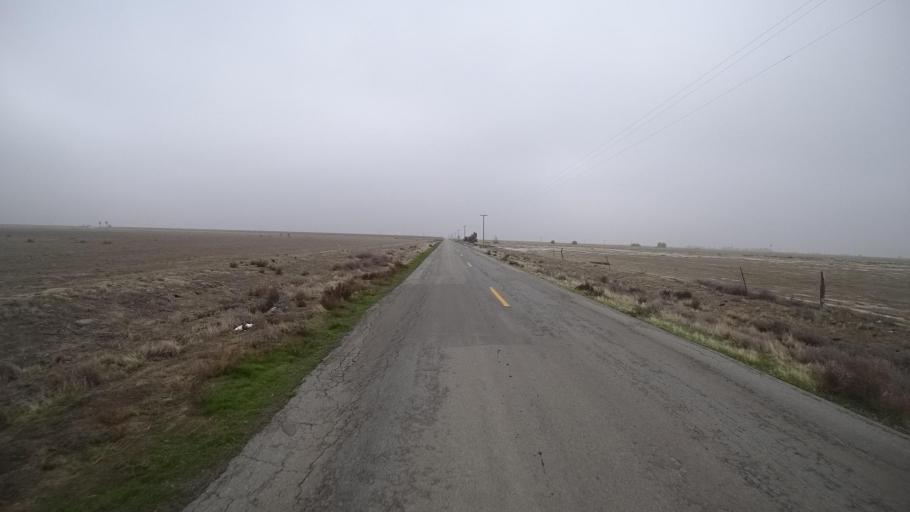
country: US
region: California
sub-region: Tulare County
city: Alpaugh
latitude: 35.7091
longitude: -119.4906
